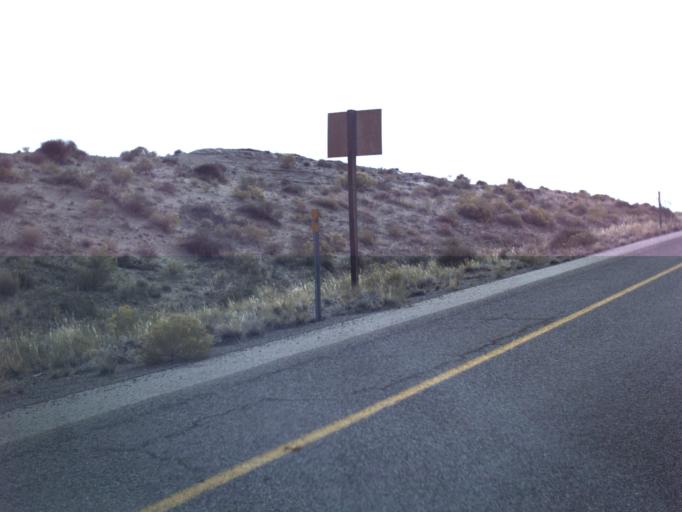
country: US
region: Utah
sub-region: Emery County
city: Ferron
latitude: 38.8333
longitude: -111.1099
